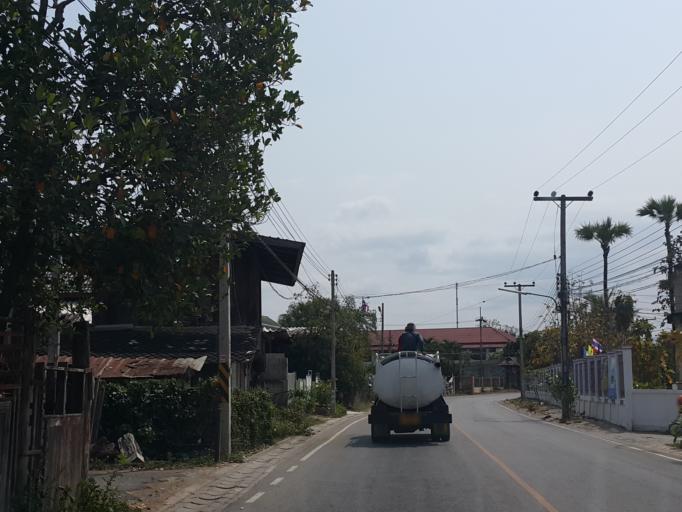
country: TH
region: Lamphun
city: Ban Thi
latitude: 18.6537
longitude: 99.1210
